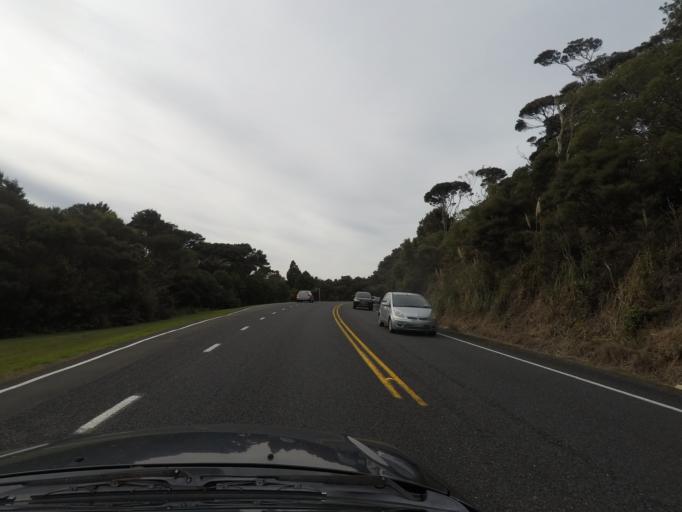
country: NZ
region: Auckland
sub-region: Auckland
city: Titirangi
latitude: -36.9460
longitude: 174.5258
